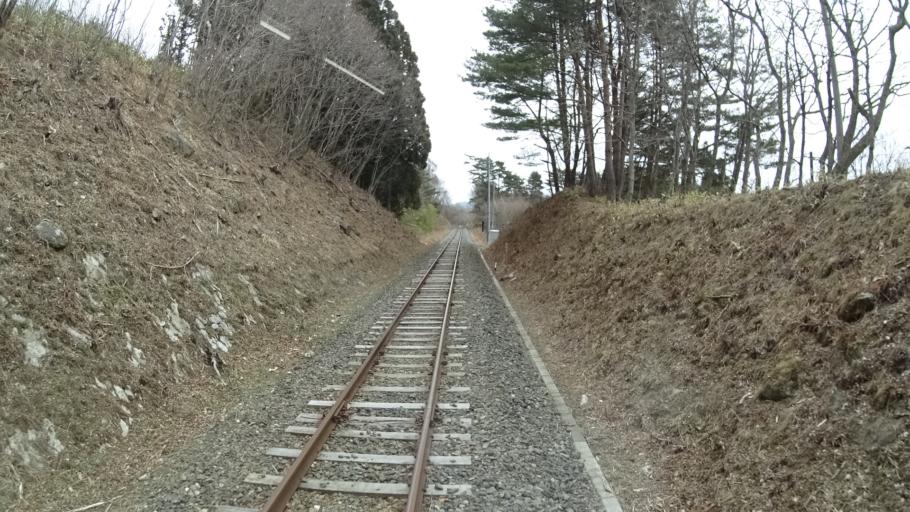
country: JP
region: Iwate
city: Otsuchi
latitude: 39.4020
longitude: 141.9523
